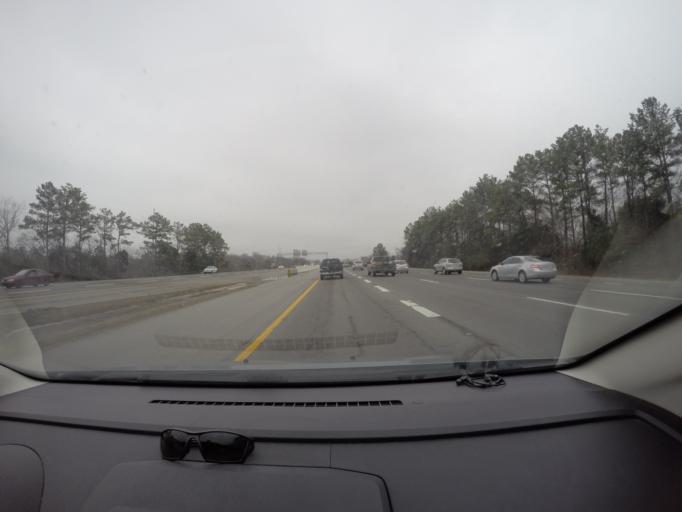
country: US
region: Tennessee
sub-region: Rutherford County
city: Murfreesboro
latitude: 35.8741
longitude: -86.4649
